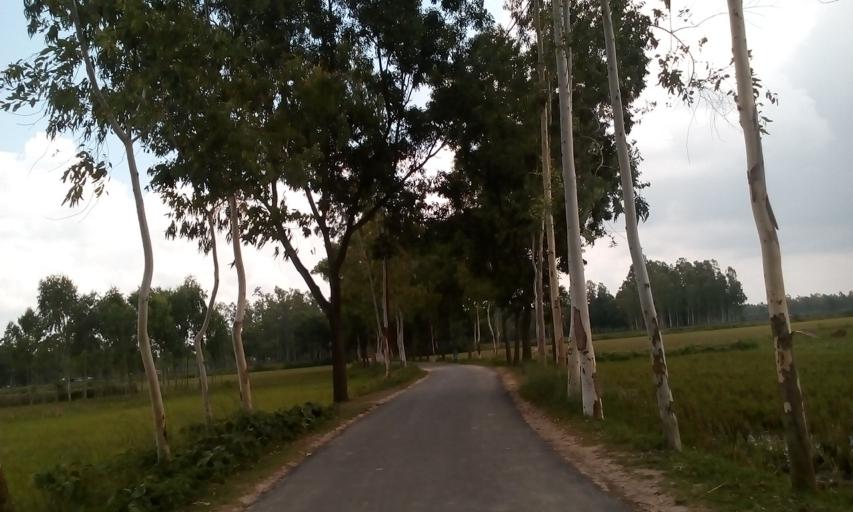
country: IN
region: West Bengal
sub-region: Dakshin Dinajpur
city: Balurghat
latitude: 25.3780
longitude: 88.9966
